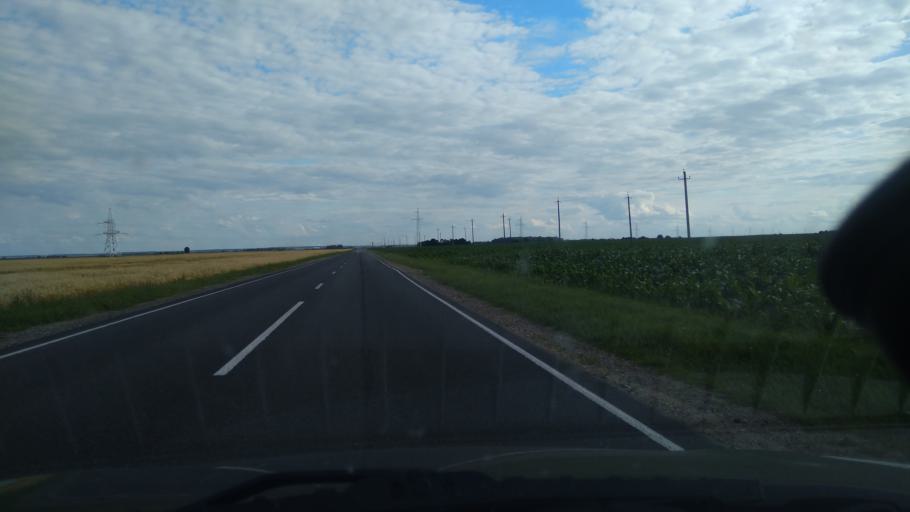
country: BY
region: Grodnenskaya
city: Masty
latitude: 53.3036
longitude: 24.6900
